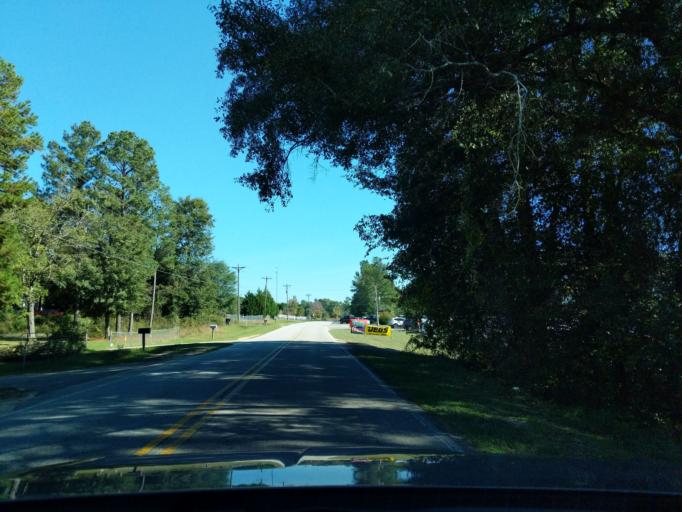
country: US
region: Georgia
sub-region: Richmond County
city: Hephzibah
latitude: 33.2588
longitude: -81.9982
